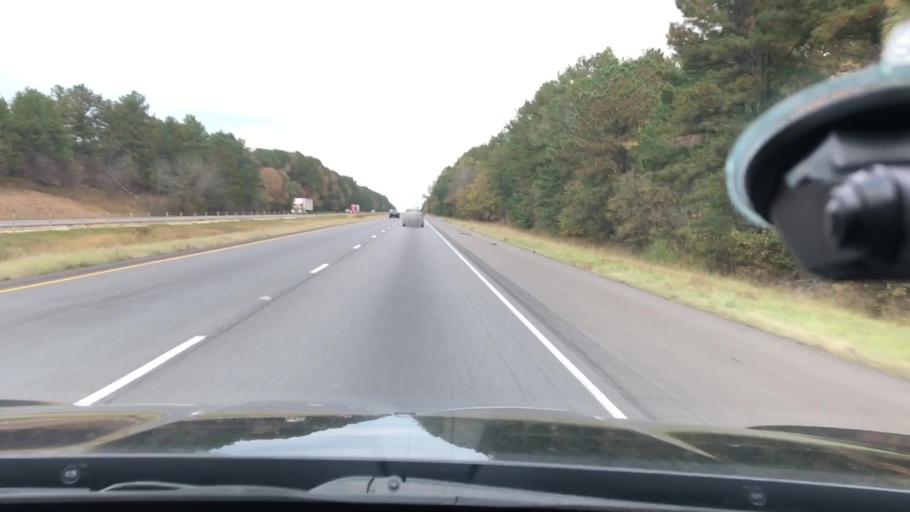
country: US
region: Arkansas
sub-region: Clark County
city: Arkadelphia
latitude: 34.2649
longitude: -92.9768
